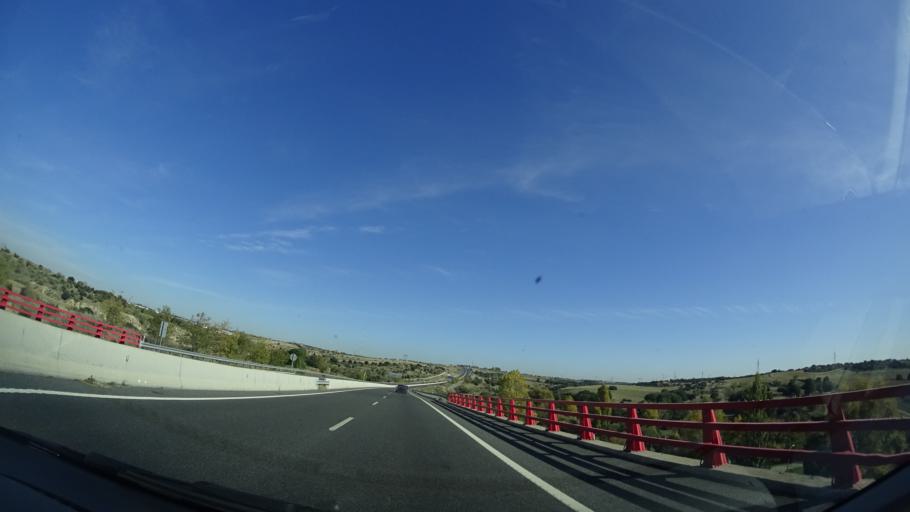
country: ES
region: Madrid
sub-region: Provincia de Madrid
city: Las Rozas de Madrid
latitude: 40.4805
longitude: -3.9156
